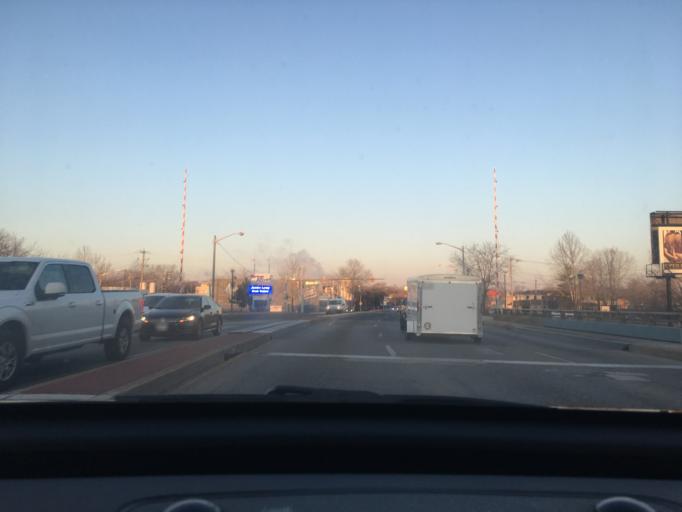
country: US
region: Maryland
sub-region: Wicomico County
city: Salisbury
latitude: 38.3661
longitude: -75.6037
